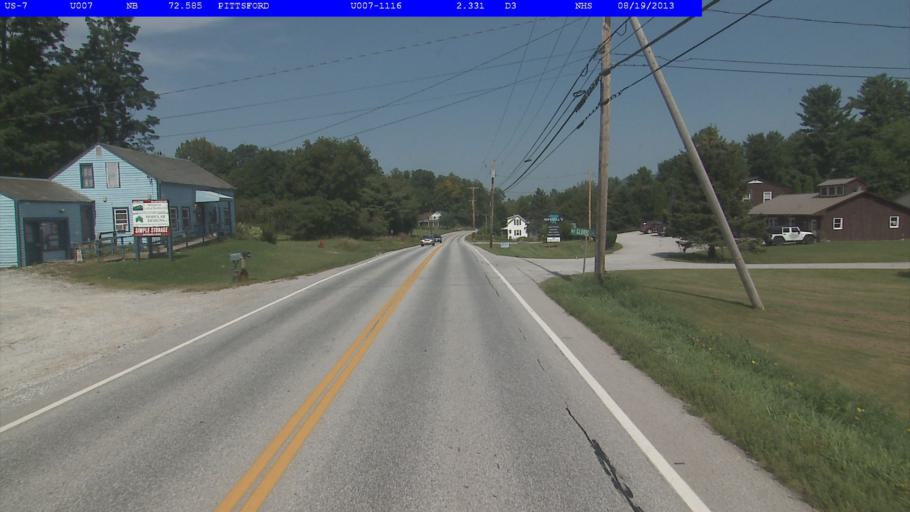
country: US
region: Vermont
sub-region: Rutland County
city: Rutland
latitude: 43.6955
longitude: -73.0034
